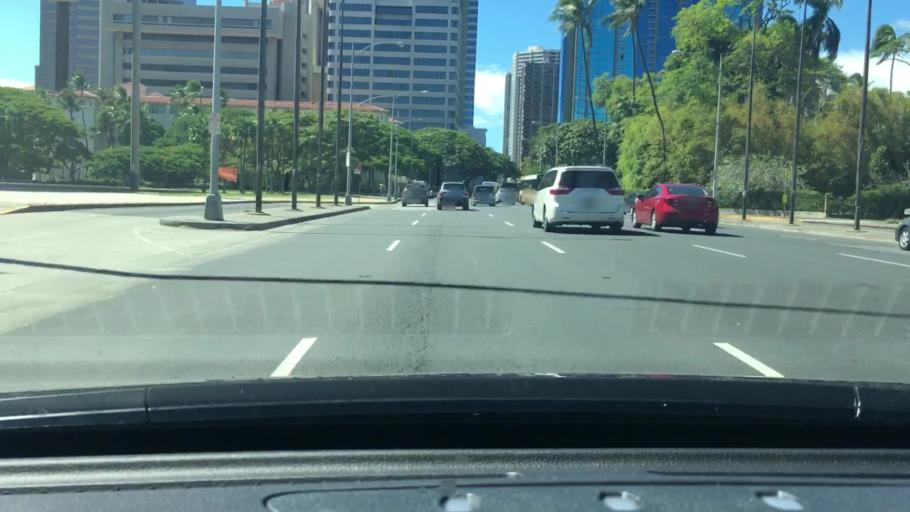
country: US
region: Hawaii
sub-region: Honolulu County
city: Honolulu
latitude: 21.3076
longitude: -157.8565
